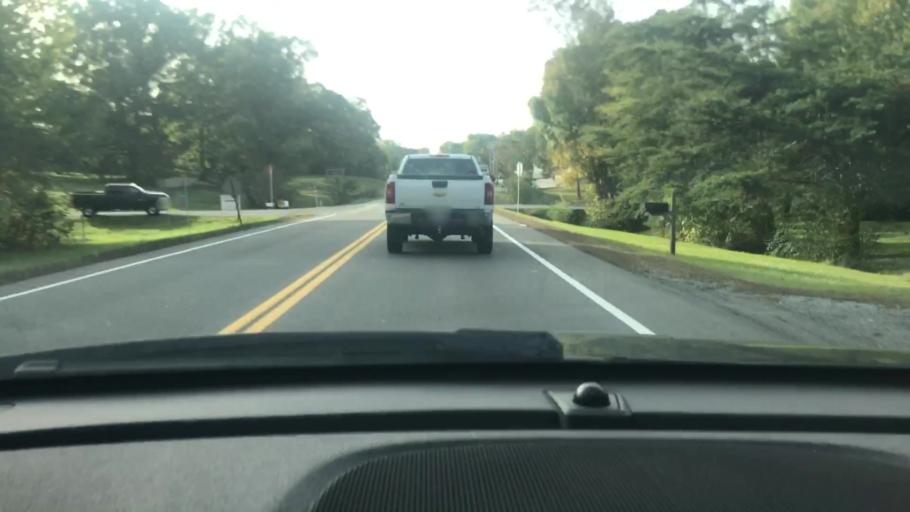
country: US
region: Tennessee
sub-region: Williamson County
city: Fairview
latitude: 36.0288
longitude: -87.1868
